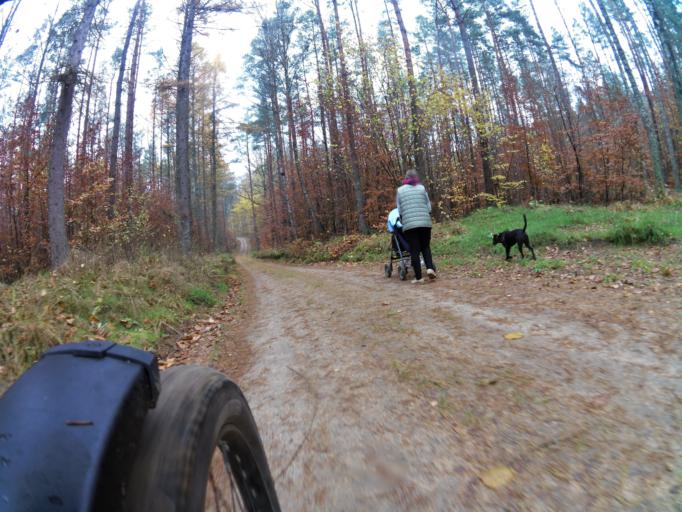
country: PL
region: Pomeranian Voivodeship
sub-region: Powiat wejherowski
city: Orle
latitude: 54.6923
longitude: 18.1563
